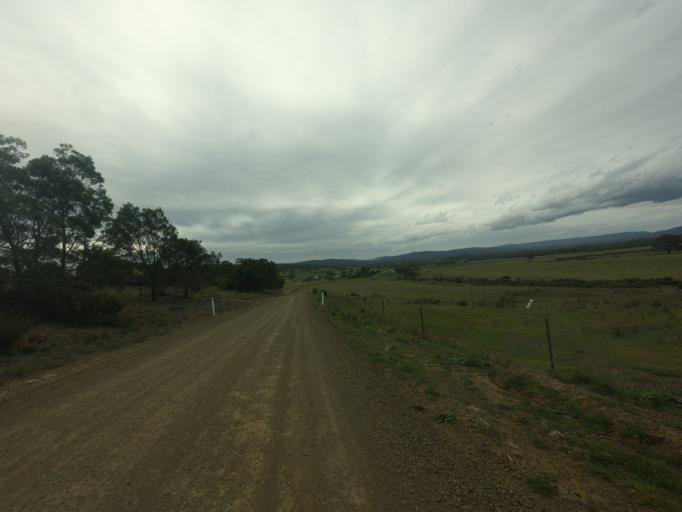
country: AU
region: Tasmania
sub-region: Break O'Day
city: St Helens
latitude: -41.9650
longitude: 148.0739
